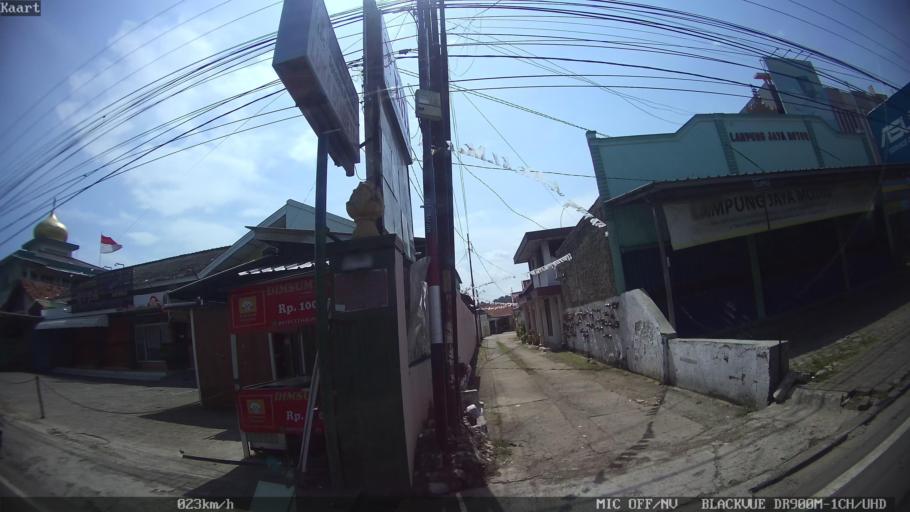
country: ID
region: Lampung
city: Kedaton
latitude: -5.4006
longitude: 105.2608
